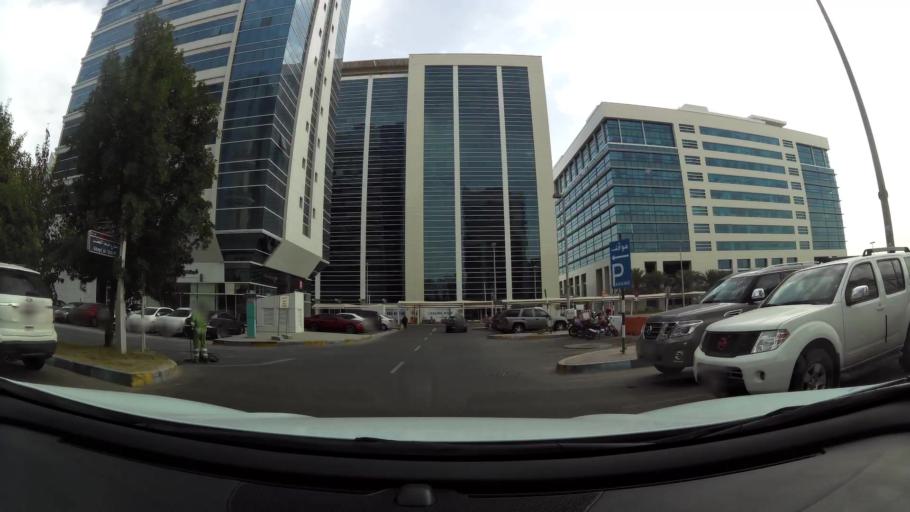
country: AE
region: Abu Dhabi
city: Abu Dhabi
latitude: 24.4632
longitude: 54.3868
